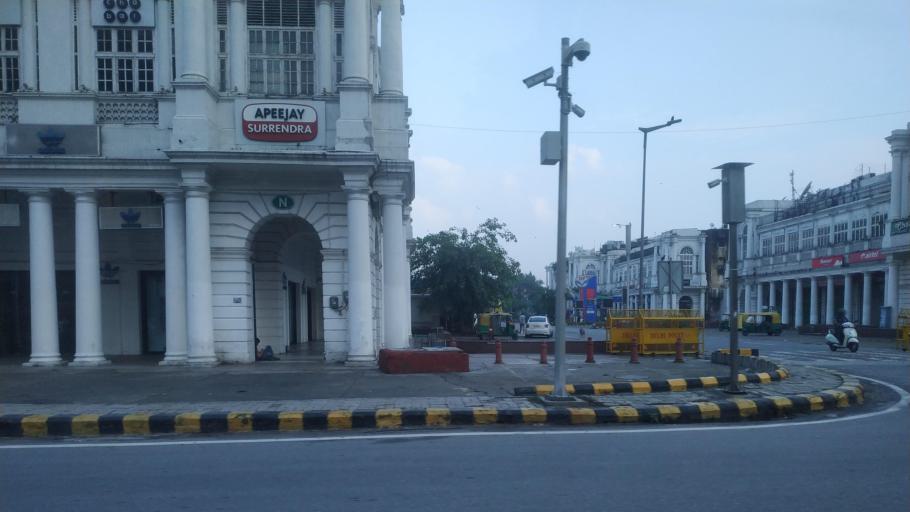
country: IN
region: NCT
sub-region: New Delhi
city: New Delhi
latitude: 28.6310
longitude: 77.2221
